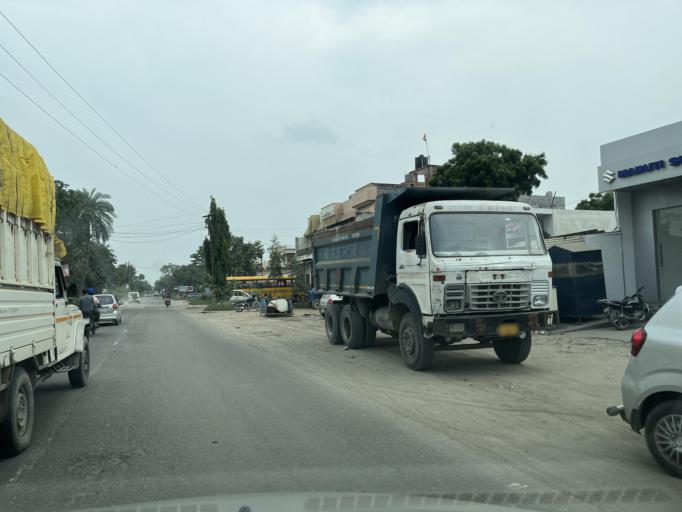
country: IN
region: Uttar Pradesh
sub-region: Rampur
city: Bilaspur
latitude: 29.0366
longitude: 79.2553
